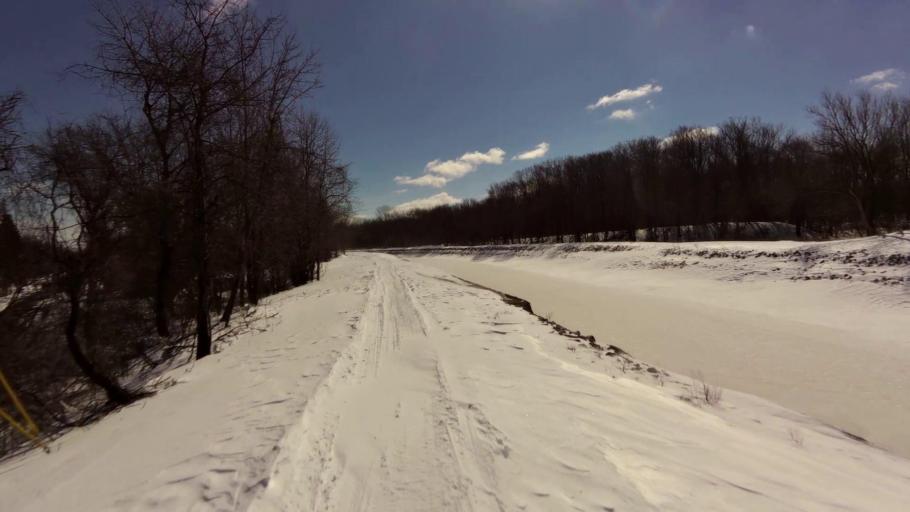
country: US
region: New York
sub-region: Orleans County
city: Holley
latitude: 43.2539
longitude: -78.0773
